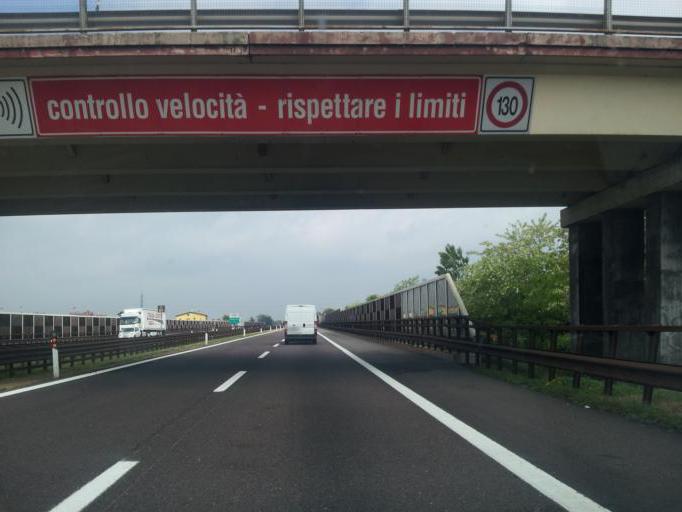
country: IT
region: Veneto
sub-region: Provincia di Verona
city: Alpo
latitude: 45.3717
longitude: 10.9166
